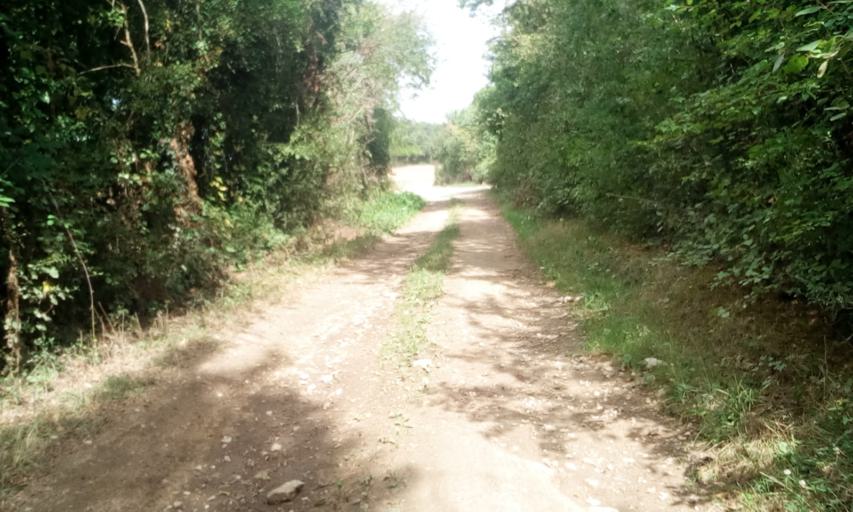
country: FR
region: Lower Normandy
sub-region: Departement du Calvados
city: Bellengreville
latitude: 49.1106
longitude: -0.2432
